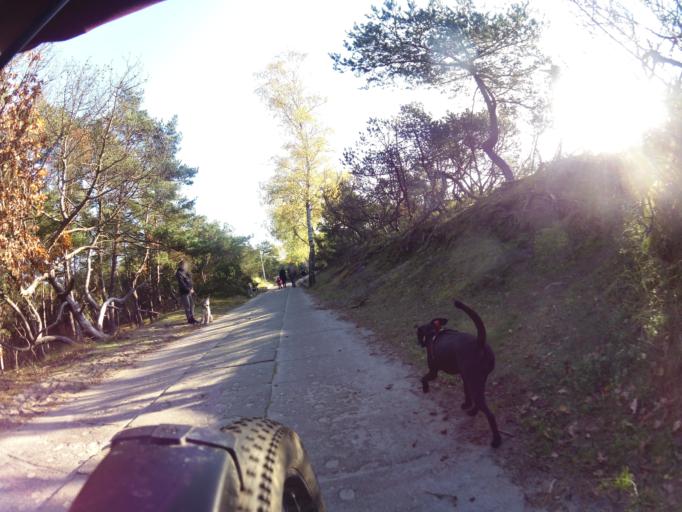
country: PL
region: Pomeranian Voivodeship
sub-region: Powiat pucki
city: Hel
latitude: 54.6024
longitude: 18.8155
